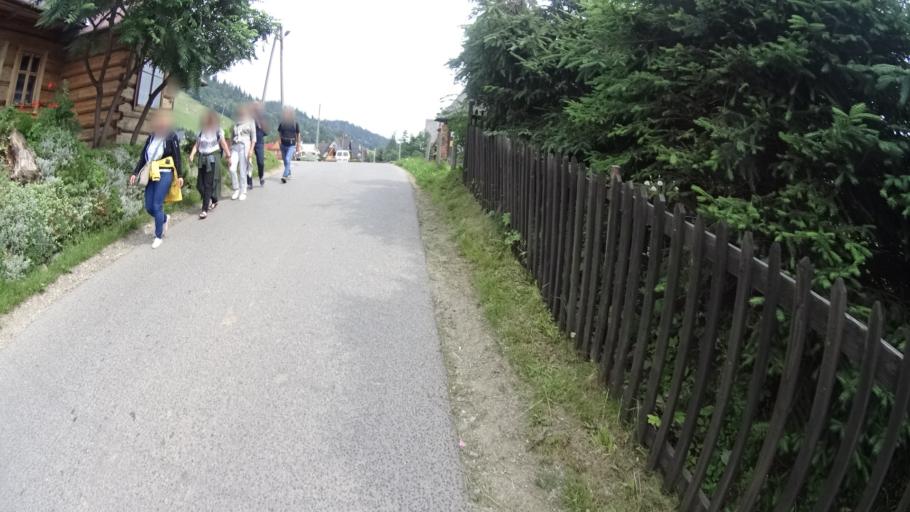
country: PL
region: Lesser Poland Voivodeship
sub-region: Powiat tatrzanski
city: Poronin
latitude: 49.3167
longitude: 19.9771
